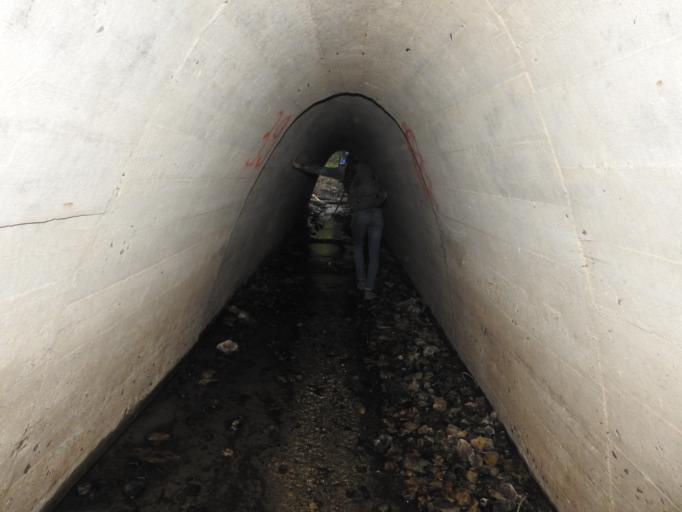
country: RU
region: Saratov
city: Sokolovyy
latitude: 51.5519
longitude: 45.8712
